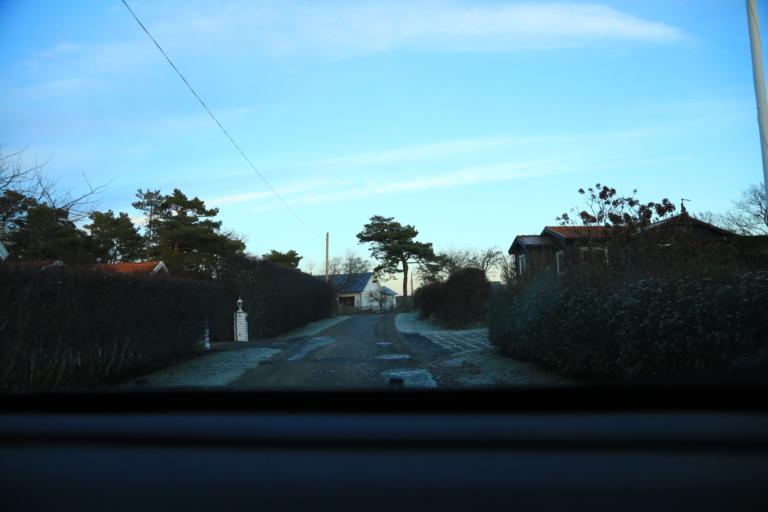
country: SE
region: Halland
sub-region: Varbergs Kommun
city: Varberg
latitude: 57.1886
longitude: 12.1752
